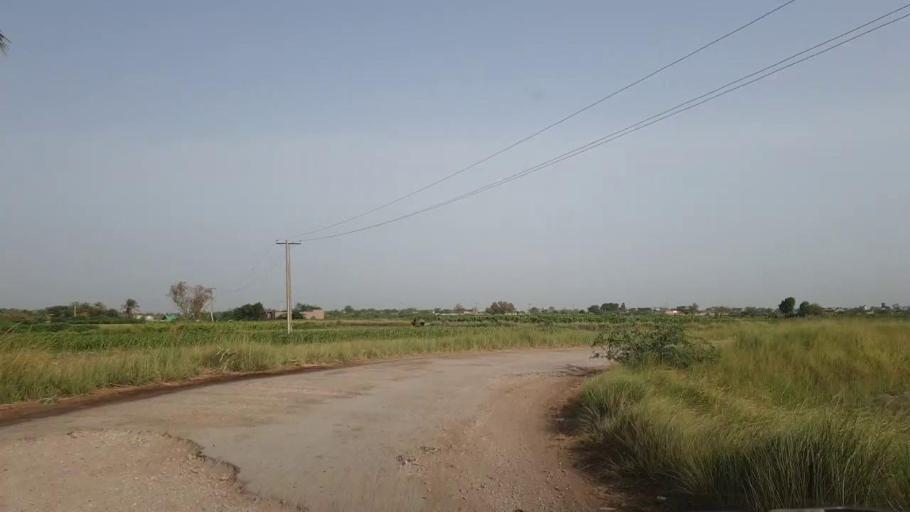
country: PK
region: Sindh
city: Nawabshah
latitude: 26.2252
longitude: 68.4054
